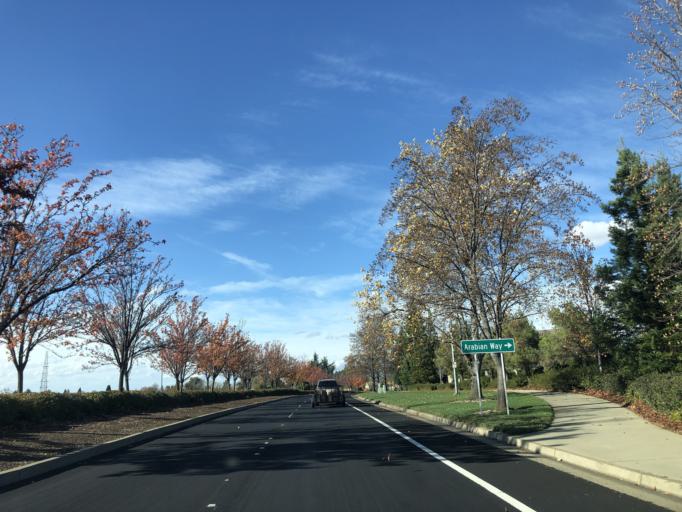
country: US
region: California
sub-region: Placer County
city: Roseville
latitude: 38.7799
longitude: -121.2908
